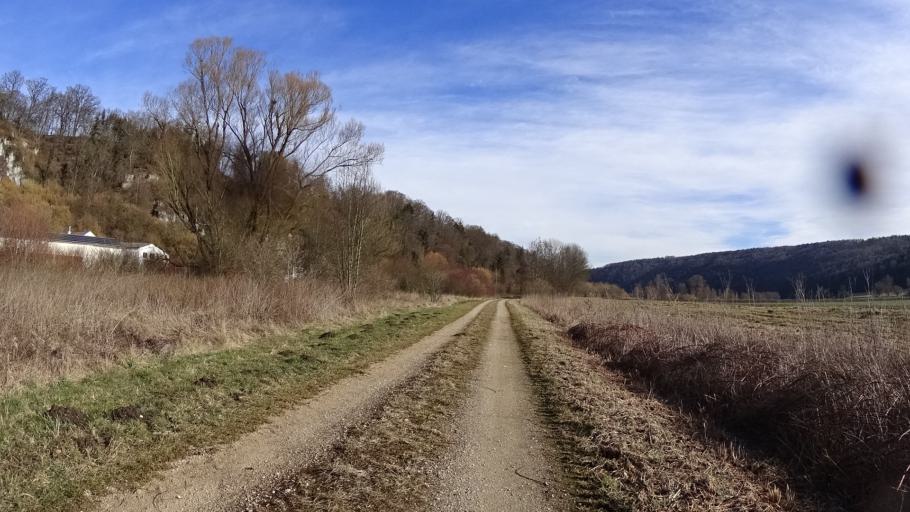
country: DE
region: Bavaria
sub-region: Upper Bavaria
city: Walting
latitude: 48.9025
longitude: 11.2882
